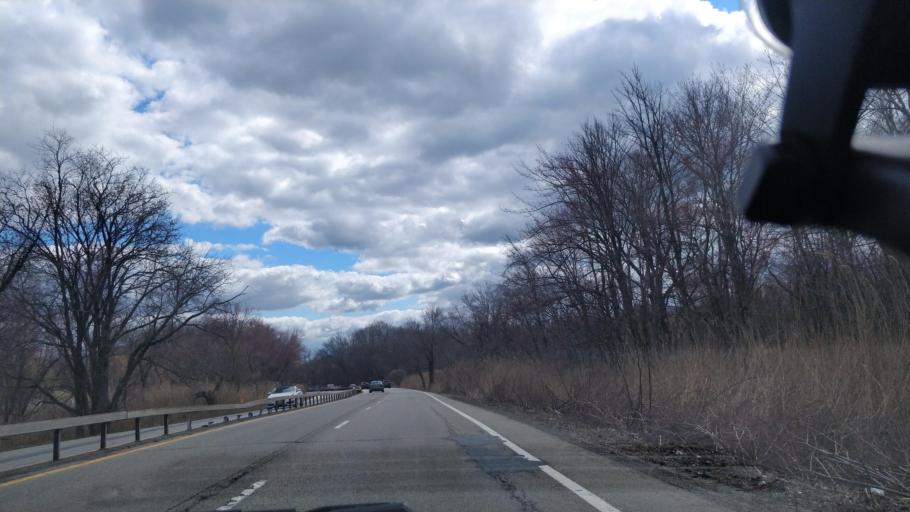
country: US
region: New York
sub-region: Westchester County
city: Ossining
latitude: 41.1647
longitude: -73.8380
